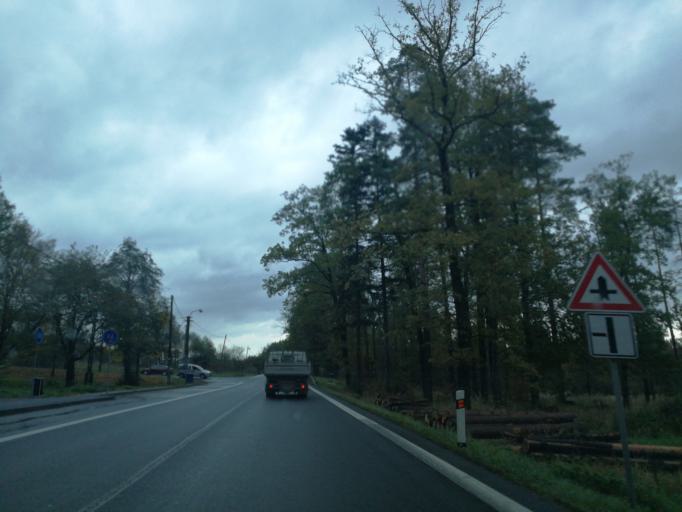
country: CZ
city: Hodslavice
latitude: 49.5235
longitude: 18.0156
